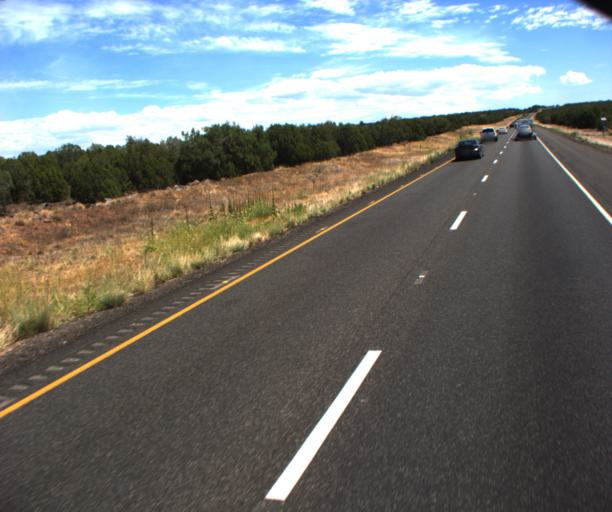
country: US
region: Arizona
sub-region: Yavapai County
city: Big Park
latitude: 34.7336
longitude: -111.6989
